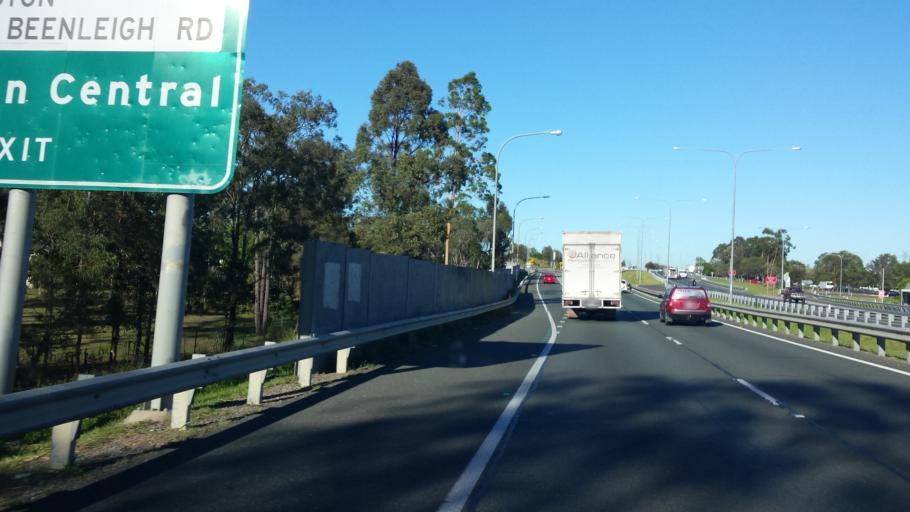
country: AU
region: Queensland
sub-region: Logan
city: Waterford West
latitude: -27.6676
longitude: 153.1275
